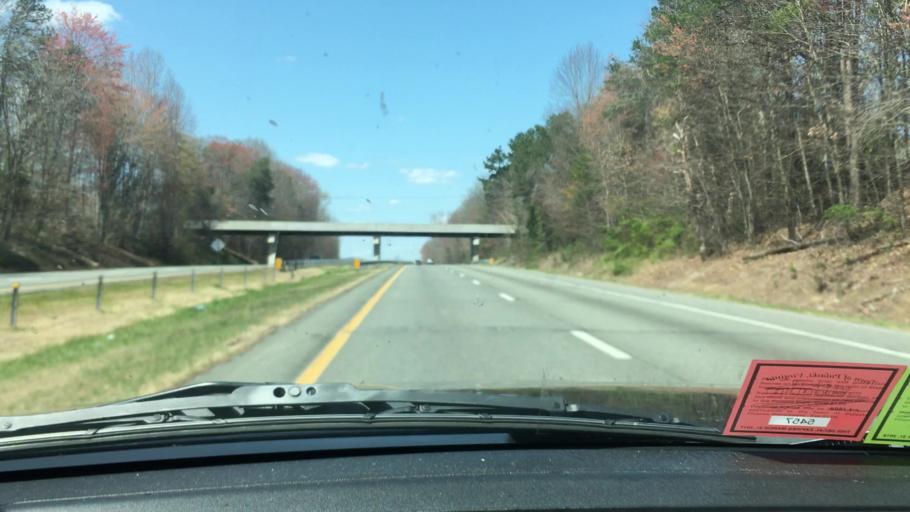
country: US
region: North Carolina
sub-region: Surry County
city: Pilot Mountain
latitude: 36.3873
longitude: -80.4898
